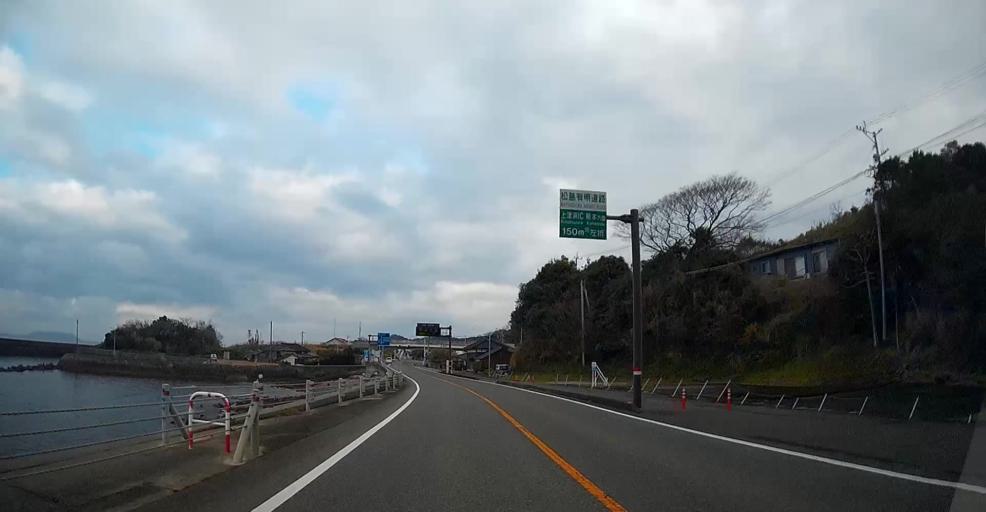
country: JP
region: Kumamoto
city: Hondo
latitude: 32.5035
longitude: 130.3014
